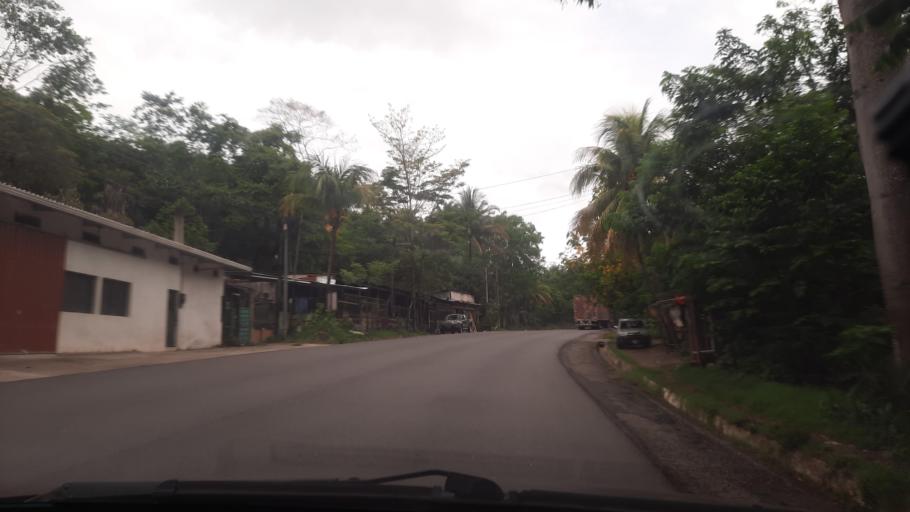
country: GT
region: Izabal
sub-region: Municipio de Los Amates
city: Los Amates
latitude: 15.2683
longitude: -89.0837
